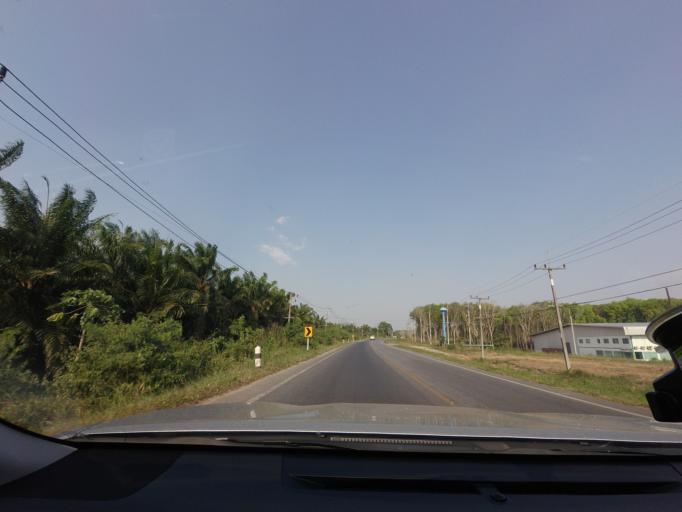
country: TH
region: Surat Thani
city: Phrasaeng
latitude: 8.5625
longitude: 99.1781
